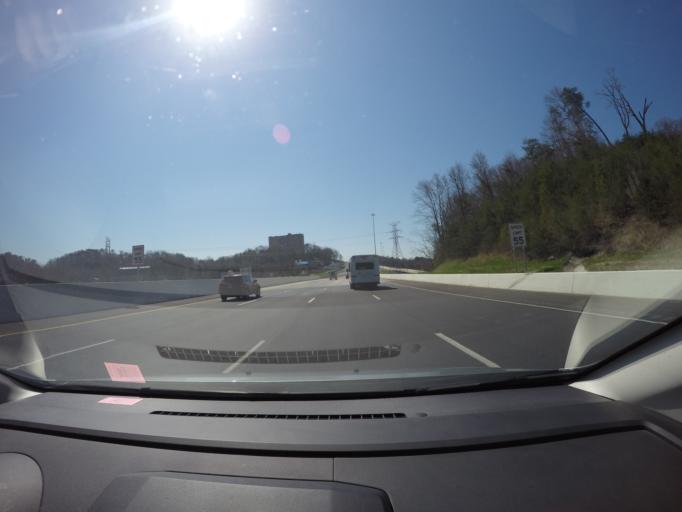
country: US
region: Tennessee
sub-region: Hamilton County
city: Chattanooga
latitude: 35.0787
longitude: -85.3220
